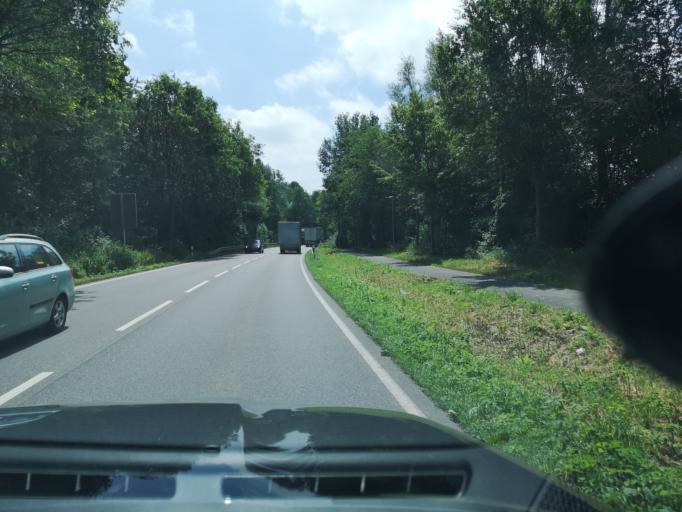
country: DE
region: North Rhine-Westphalia
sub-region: Regierungsbezirk Munster
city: Isselburg
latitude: 51.8397
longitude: 6.4530
